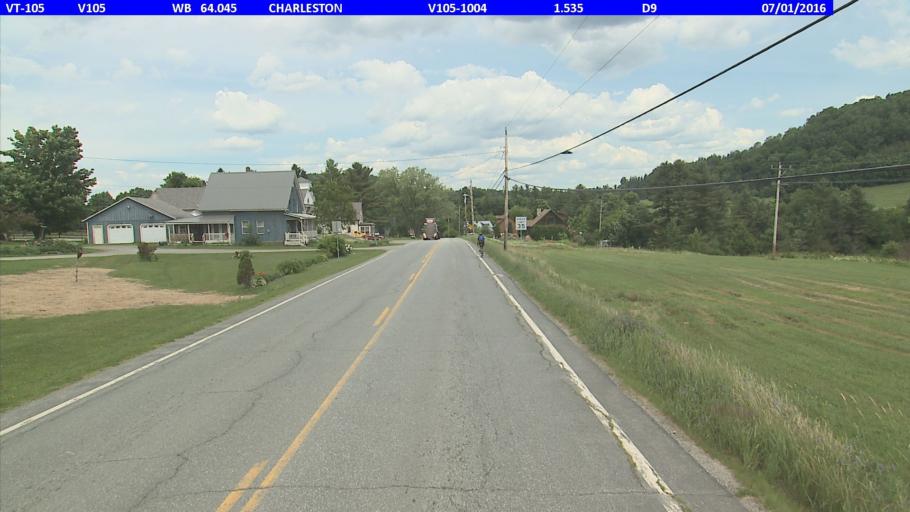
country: US
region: Vermont
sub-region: Orleans County
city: Newport
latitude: 44.8930
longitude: -72.0561
